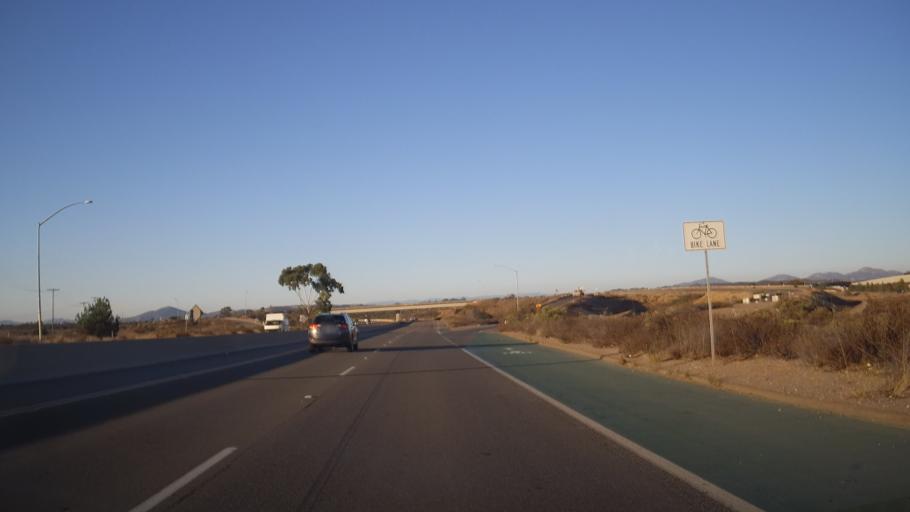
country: US
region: California
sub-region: San Diego County
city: La Mesa
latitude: 32.8575
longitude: -117.1179
